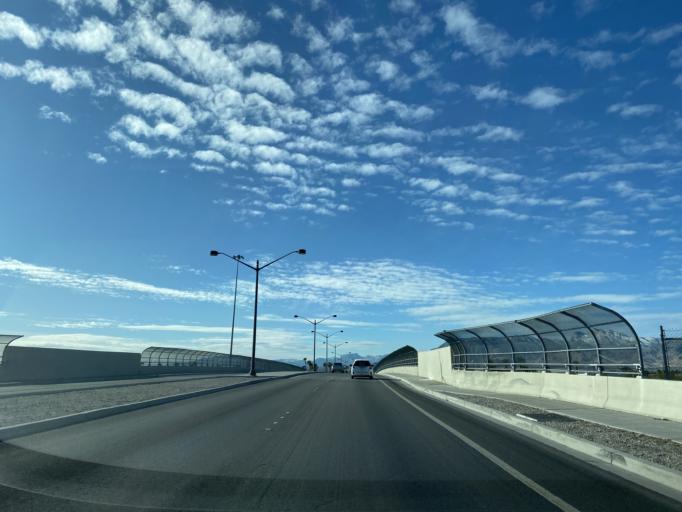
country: US
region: Nevada
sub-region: Clark County
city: Las Vegas
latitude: 36.2737
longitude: -115.2618
